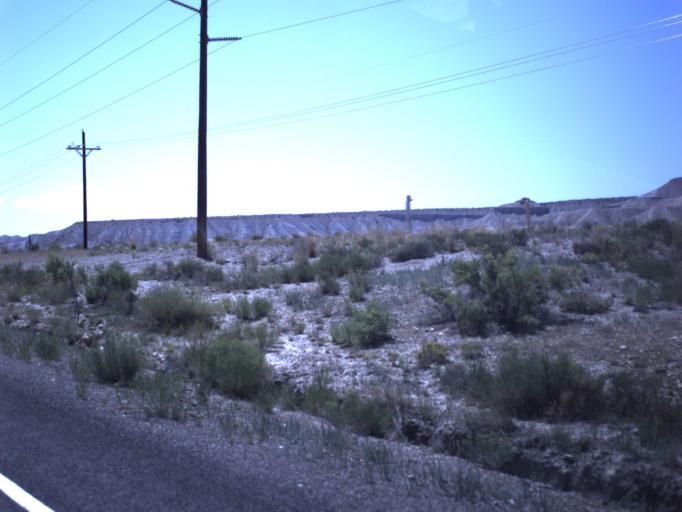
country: US
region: Utah
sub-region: Emery County
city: Orangeville
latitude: 39.2465
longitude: -111.0930
